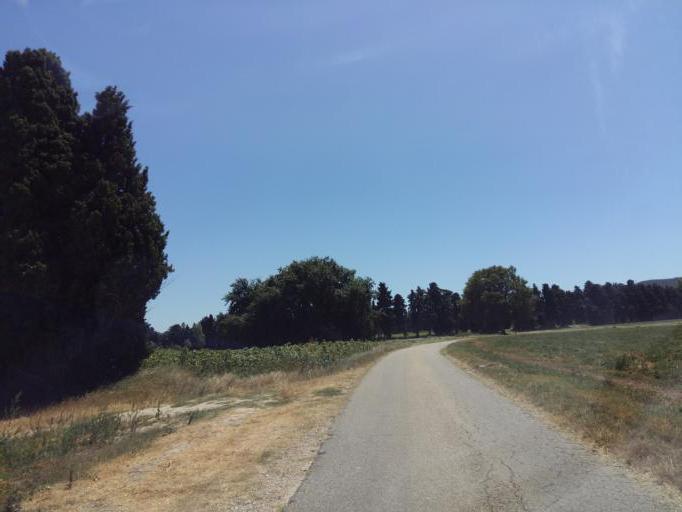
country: FR
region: Provence-Alpes-Cote d'Azur
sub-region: Departement du Vaucluse
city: Mornas
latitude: 44.1788
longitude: 4.7277
